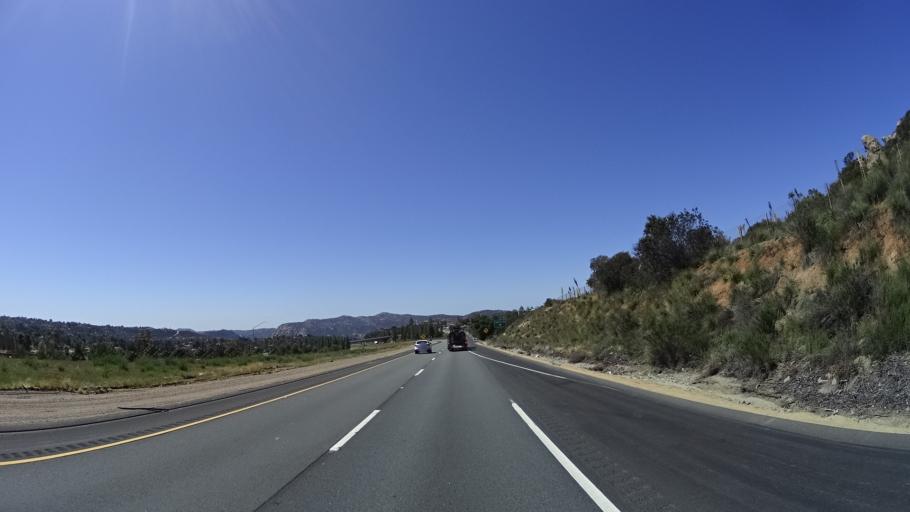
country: US
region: California
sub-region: San Diego County
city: Alpine
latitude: 32.8402
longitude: -116.7731
